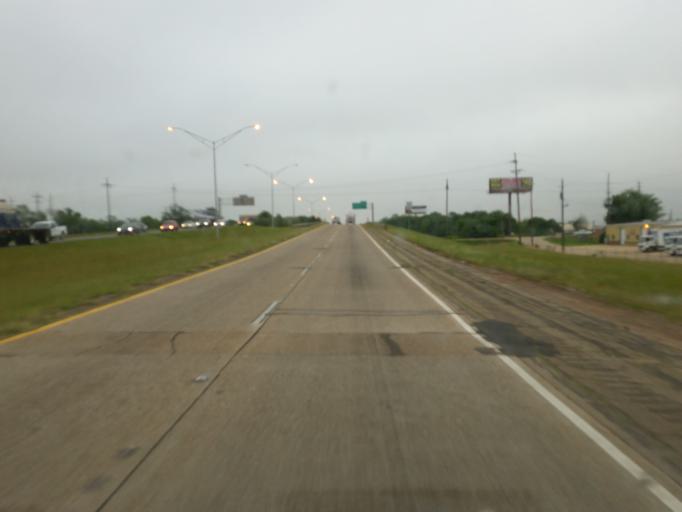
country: US
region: Louisiana
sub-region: Bossier Parish
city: Bossier City
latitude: 32.5258
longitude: -93.6934
